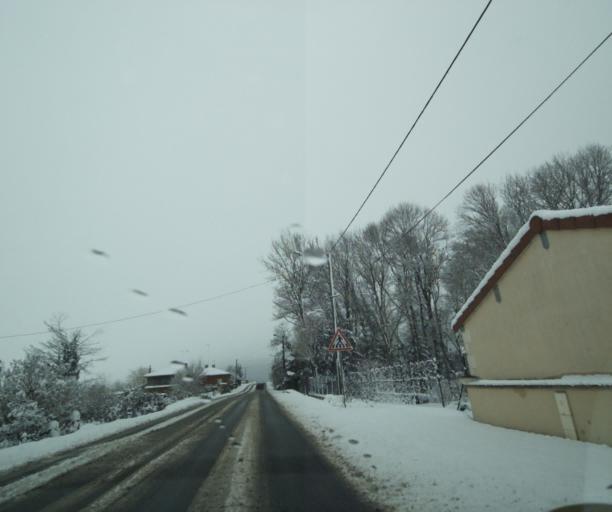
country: FR
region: Champagne-Ardenne
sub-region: Departement de la Haute-Marne
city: Wassy
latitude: 48.5470
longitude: 4.9240
